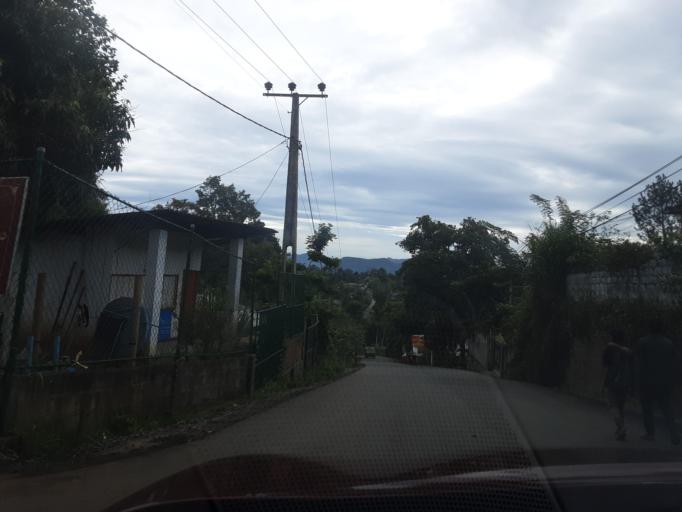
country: LK
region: Uva
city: Haputale
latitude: 6.8349
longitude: 80.9935
